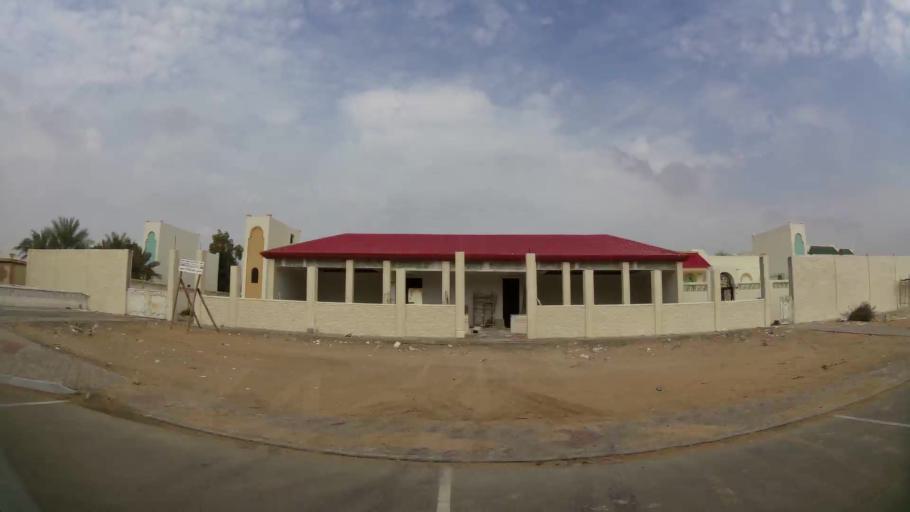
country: AE
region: Abu Dhabi
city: Abu Dhabi
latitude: 24.6421
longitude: 54.7283
